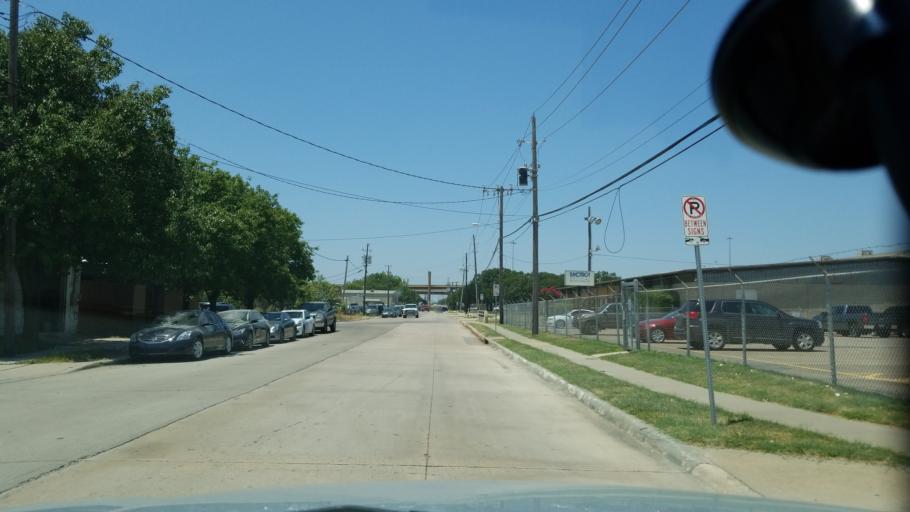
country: US
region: Texas
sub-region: Dallas County
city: Farmers Branch
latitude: 32.8929
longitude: -96.8935
